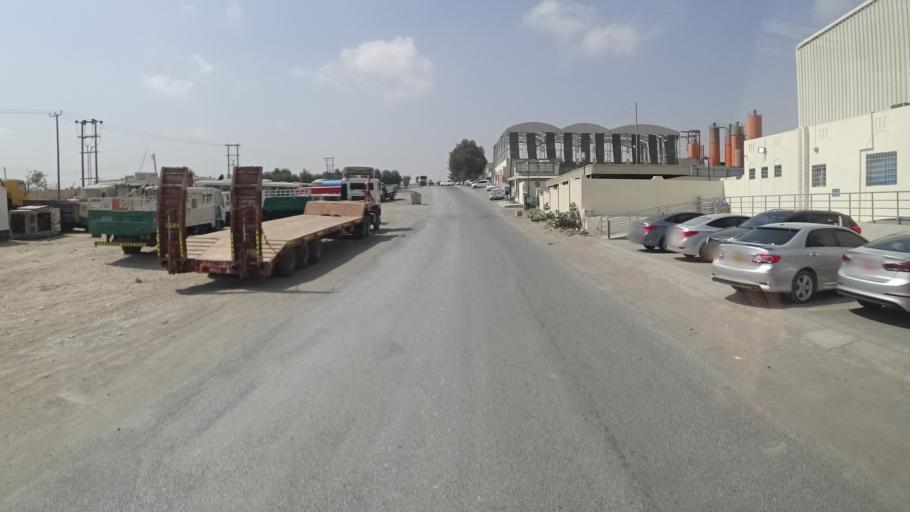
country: OM
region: Muhafazat Masqat
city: Bawshar
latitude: 23.5719
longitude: 58.3457
